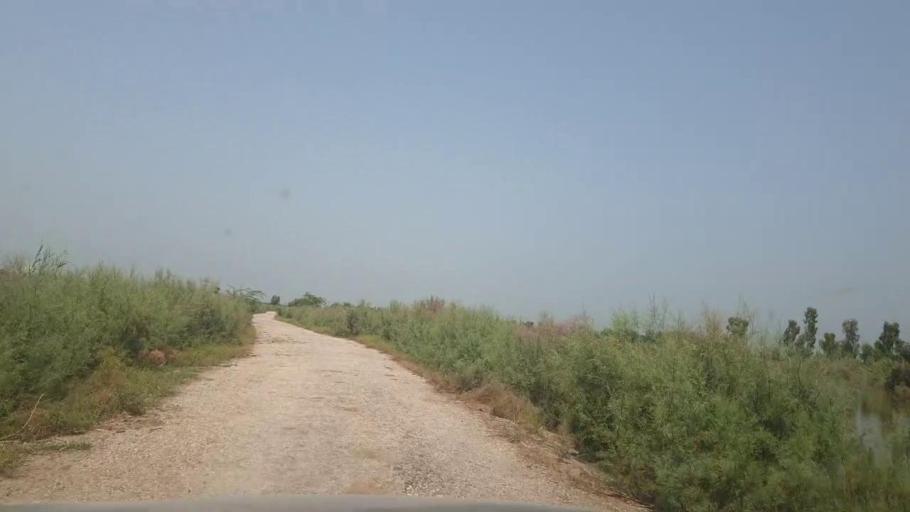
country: PK
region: Sindh
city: Lakhi
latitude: 27.8515
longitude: 68.6242
